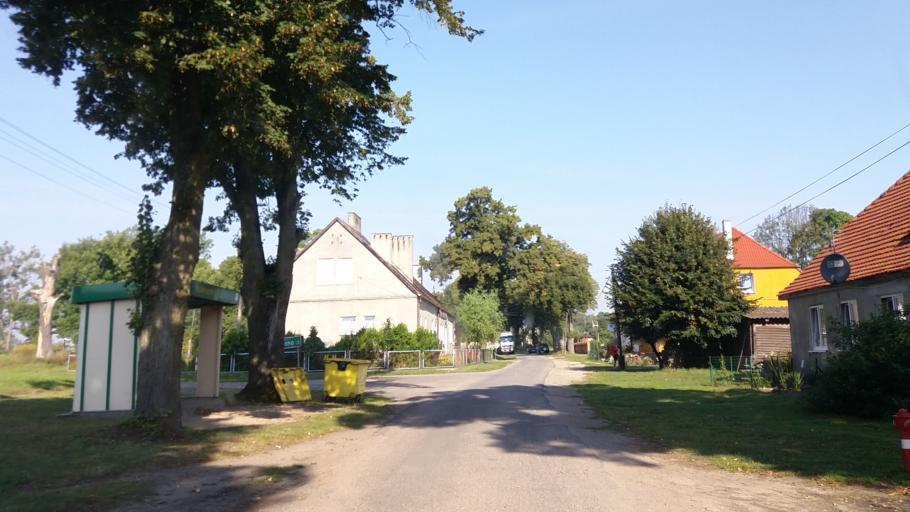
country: PL
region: West Pomeranian Voivodeship
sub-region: Powiat choszczenski
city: Pelczyce
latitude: 52.9825
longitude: 15.3331
